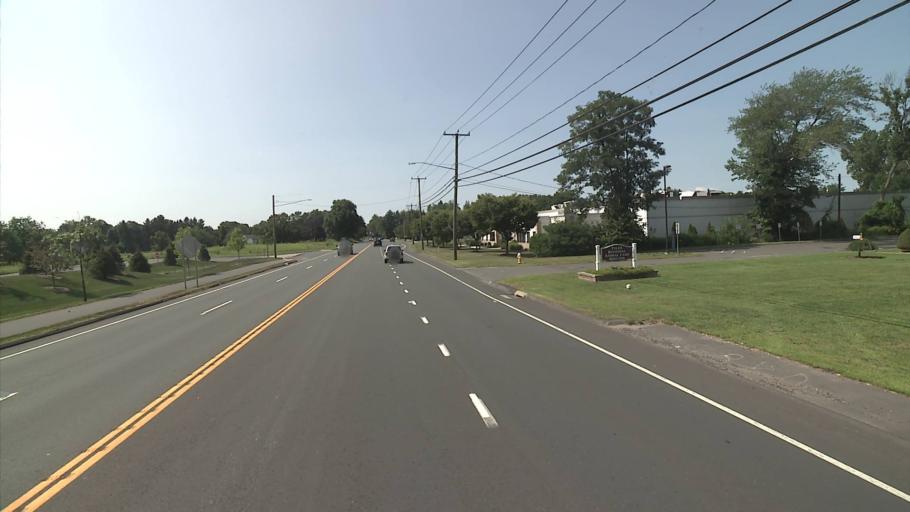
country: US
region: Connecticut
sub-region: Hartford County
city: South Windsor
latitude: 41.8569
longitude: -72.5986
